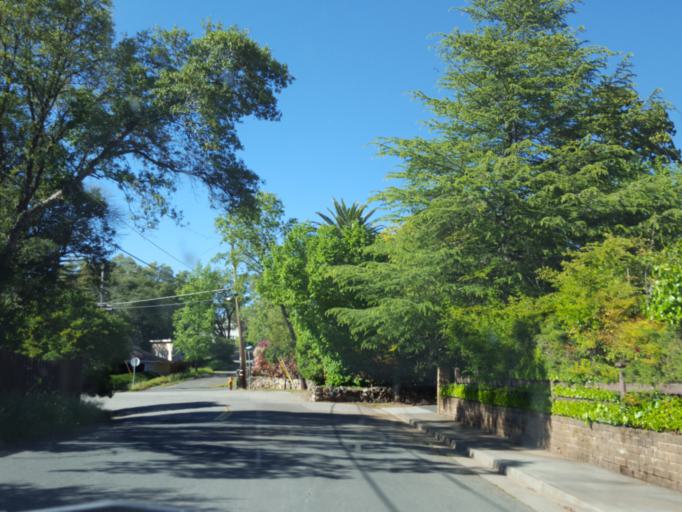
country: US
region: California
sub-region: Placer County
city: Auburn
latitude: 38.8956
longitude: -121.0616
